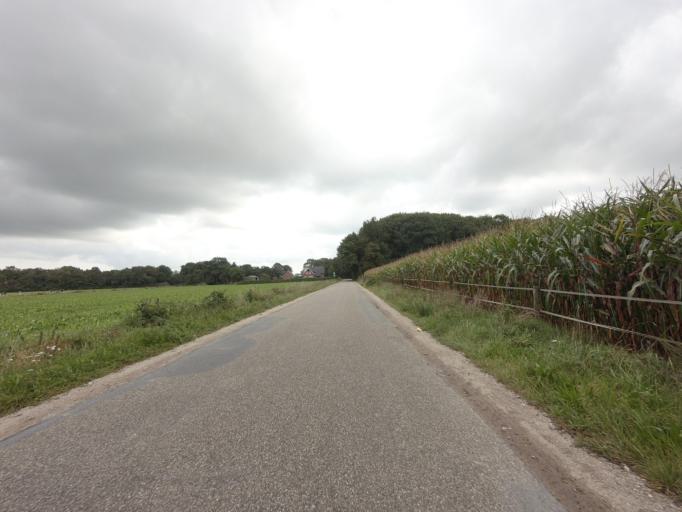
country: NL
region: Overijssel
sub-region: Gemeente Losser
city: Losser
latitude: 52.2596
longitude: 7.0233
